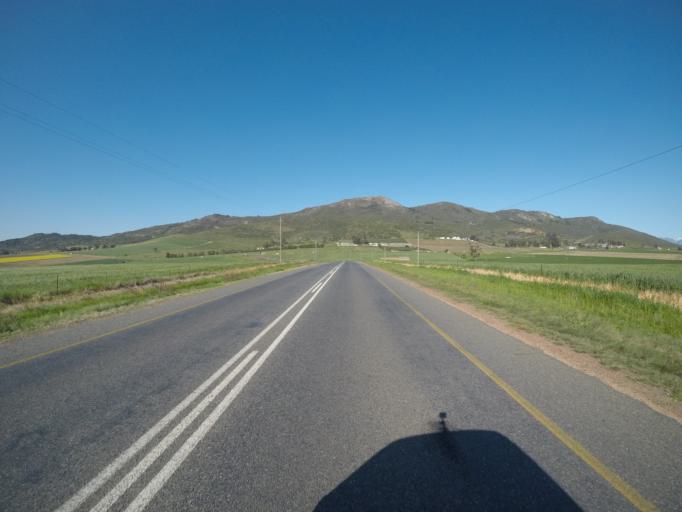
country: ZA
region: Western Cape
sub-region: Cape Winelands District Municipality
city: Noorder-Paarl
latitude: -33.7078
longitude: 18.8863
